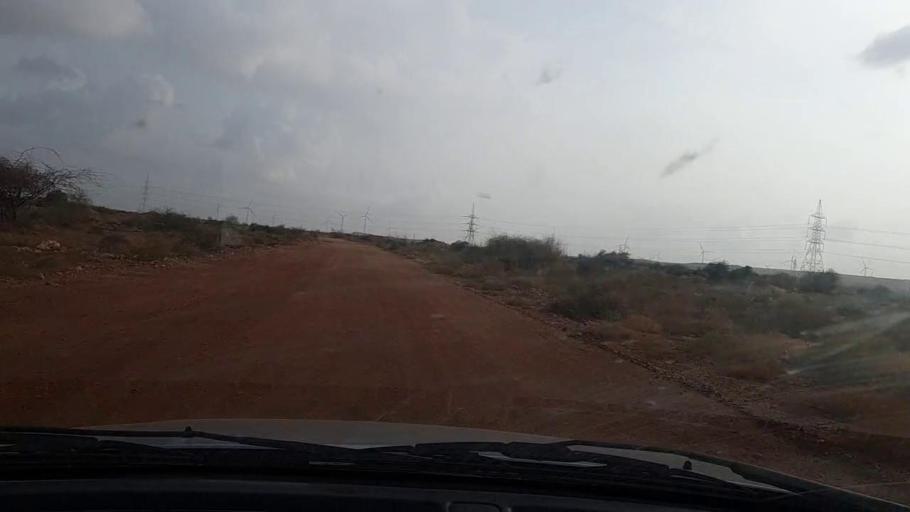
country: PK
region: Sindh
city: Thatta
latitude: 25.0635
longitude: 67.8856
